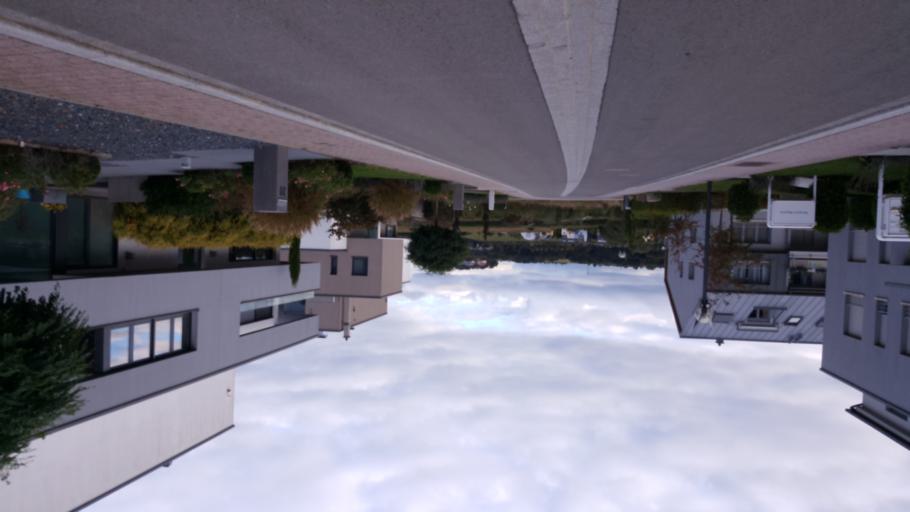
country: LU
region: Luxembourg
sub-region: Canton de Luxembourg
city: Alzingen
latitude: 49.5692
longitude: 6.1682
